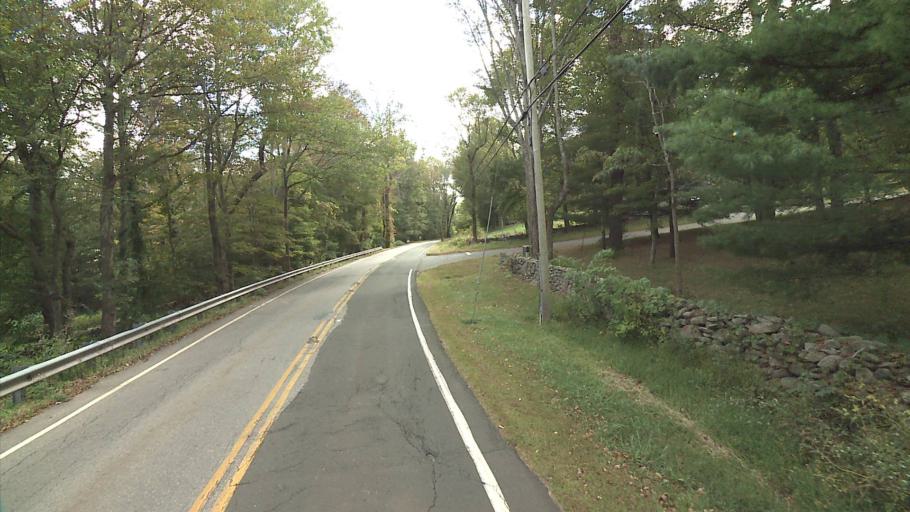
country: US
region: Connecticut
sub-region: Middlesex County
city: Higganum
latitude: 41.4077
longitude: -72.6075
